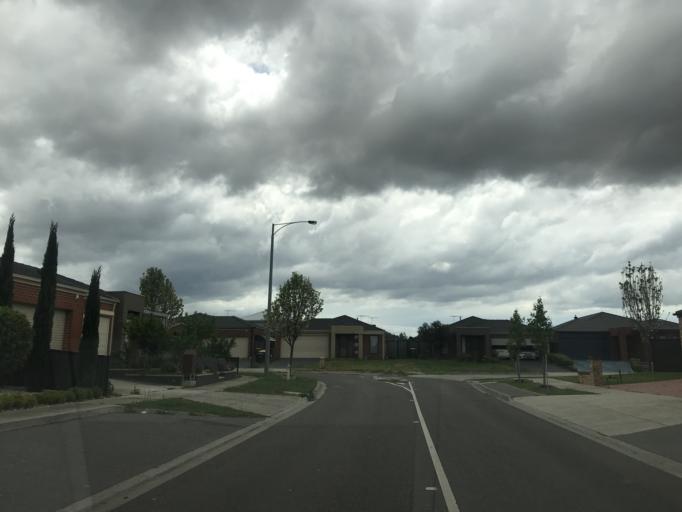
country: AU
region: Victoria
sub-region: Brimbank
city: Derrimut
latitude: -37.7864
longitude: 144.7566
